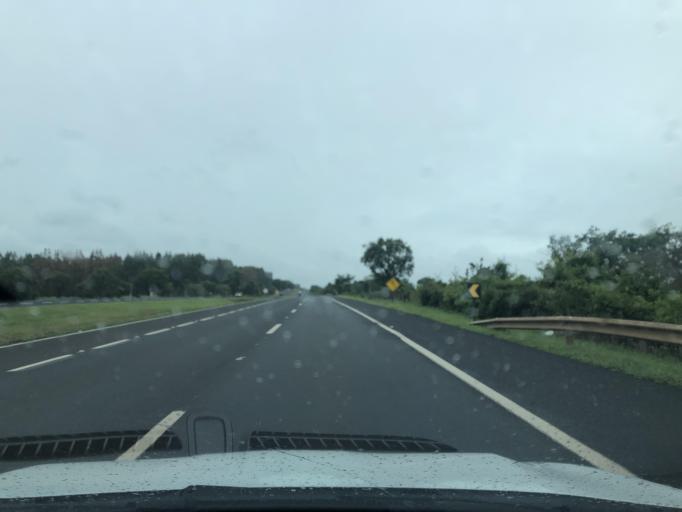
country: BR
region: Minas Gerais
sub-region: Uberaba
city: Uberaba
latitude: -19.4785
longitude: -48.0531
